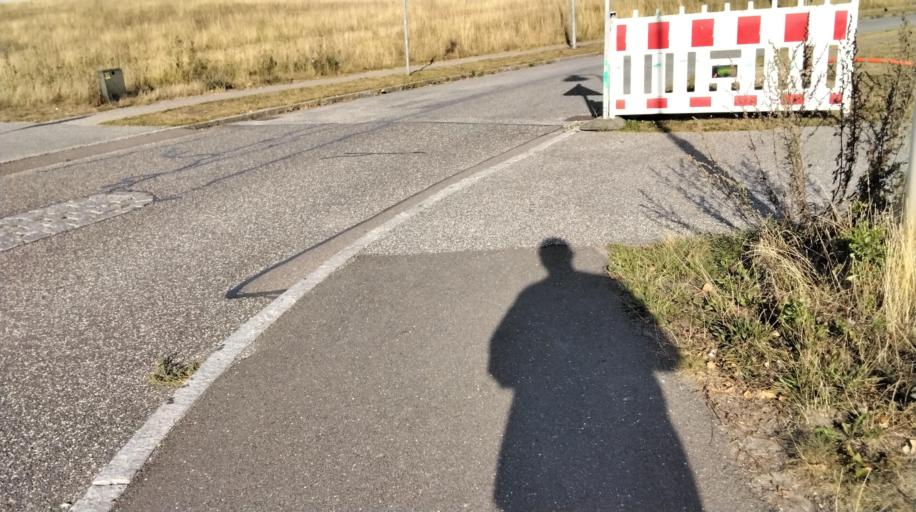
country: DK
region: Zealand
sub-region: Naestved Kommune
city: Naestved
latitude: 55.2283
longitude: 11.7306
